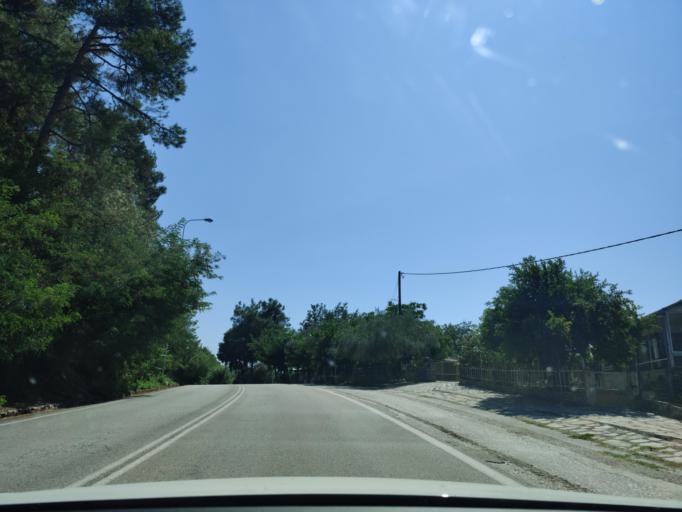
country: GR
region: East Macedonia and Thrace
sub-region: Nomos Kavalas
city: Zygos
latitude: 41.0079
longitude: 24.3829
